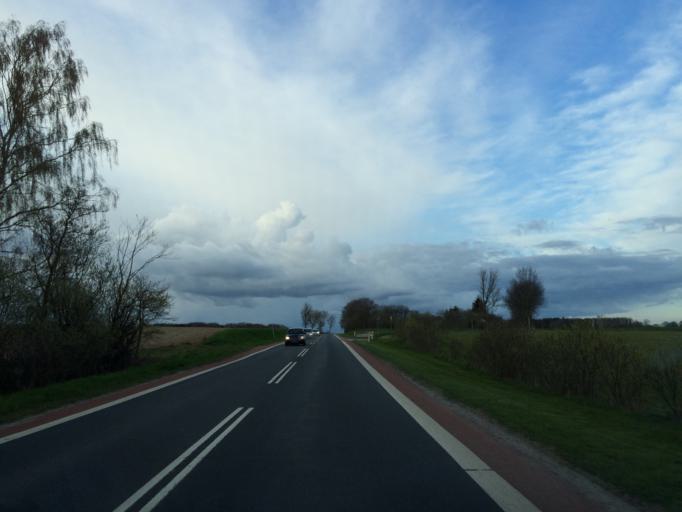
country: DK
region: South Denmark
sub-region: Odense Kommune
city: Bellinge
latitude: 55.2943
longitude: 10.2863
